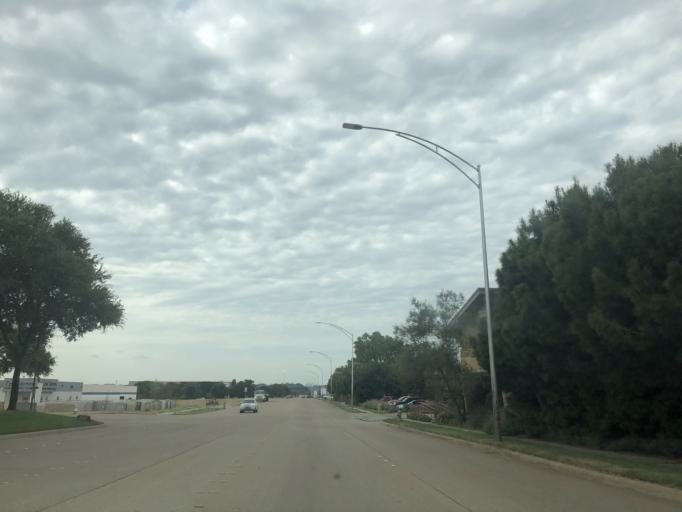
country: US
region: Texas
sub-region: Tarrant County
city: Richland Hills
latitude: 32.7936
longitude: -97.2212
